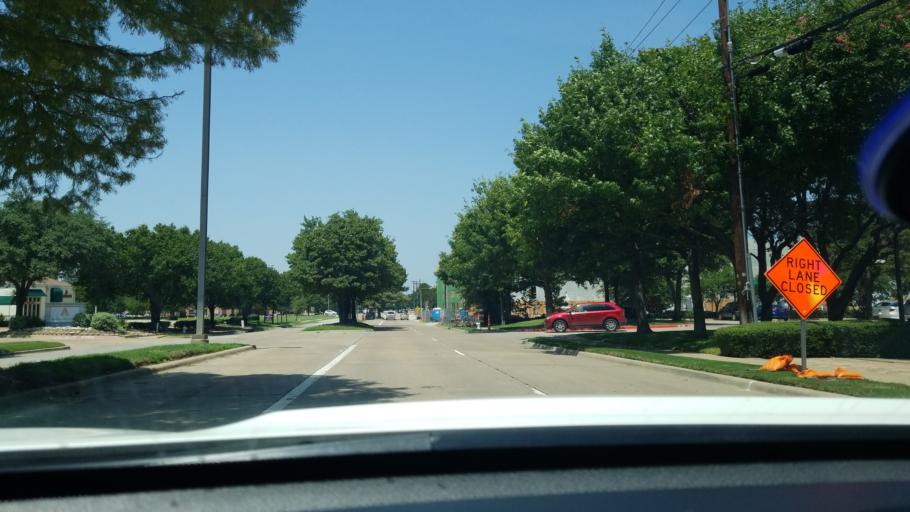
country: US
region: Texas
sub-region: Dallas County
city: Addison
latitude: 32.9555
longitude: -96.8261
